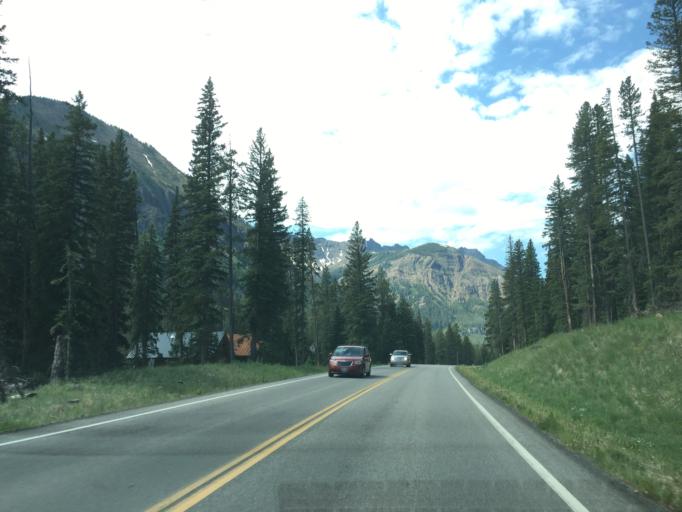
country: US
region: Montana
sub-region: Stillwater County
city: Absarokee
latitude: 45.0121
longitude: -109.9741
